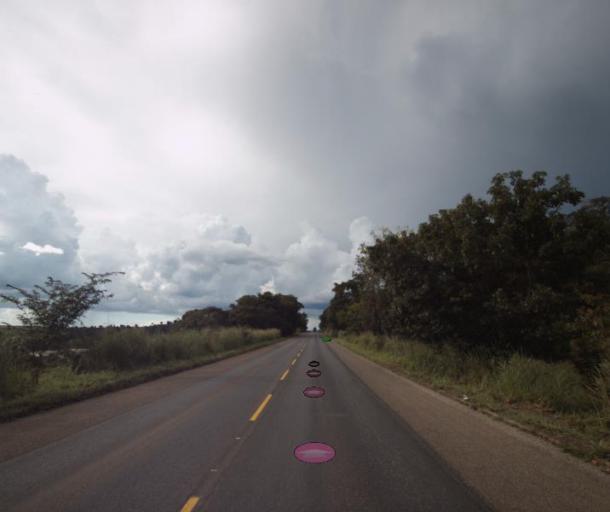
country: BR
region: Goias
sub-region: Ceres
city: Ceres
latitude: -15.1922
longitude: -49.5449
